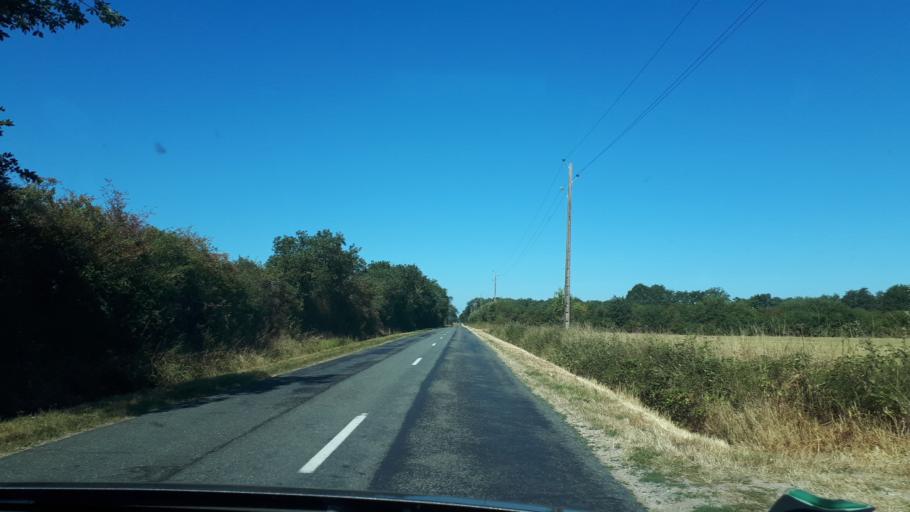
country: FR
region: Centre
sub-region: Departement du Loiret
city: Coullons
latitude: 47.6293
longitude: 2.4753
